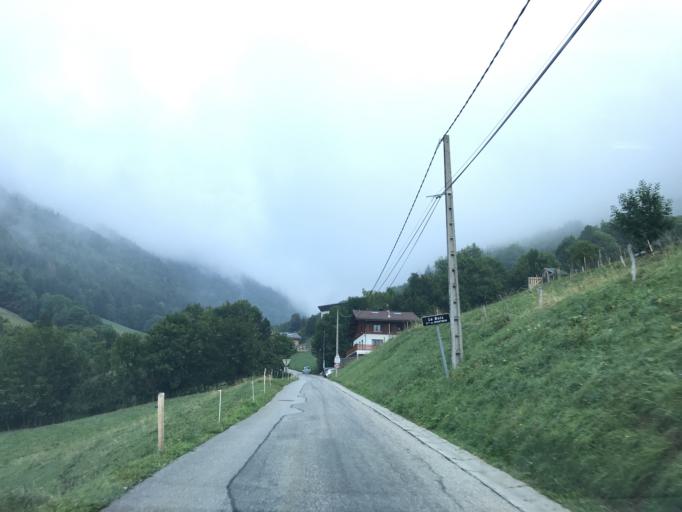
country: FR
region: Rhone-Alpes
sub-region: Departement de la Haute-Savoie
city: Doussard
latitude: 45.8094
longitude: 6.2620
